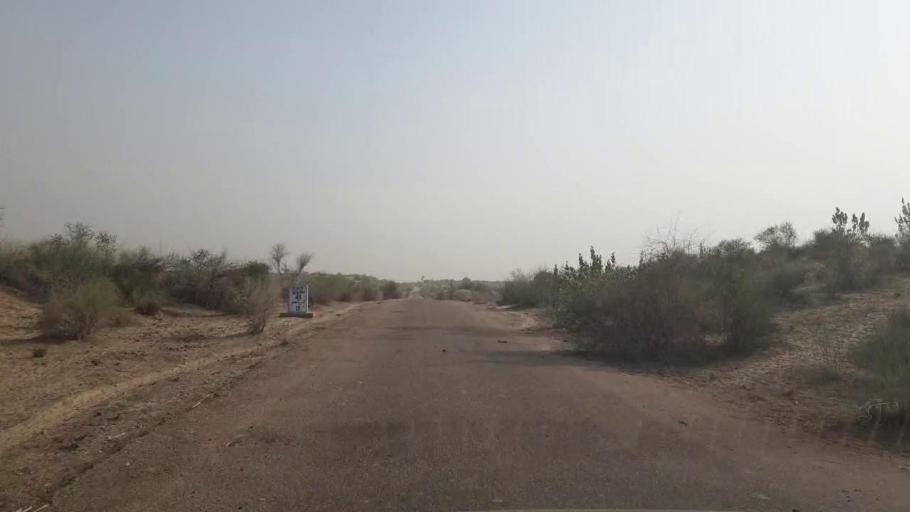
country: PK
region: Sindh
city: Chor
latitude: 25.5005
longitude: 69.9697
